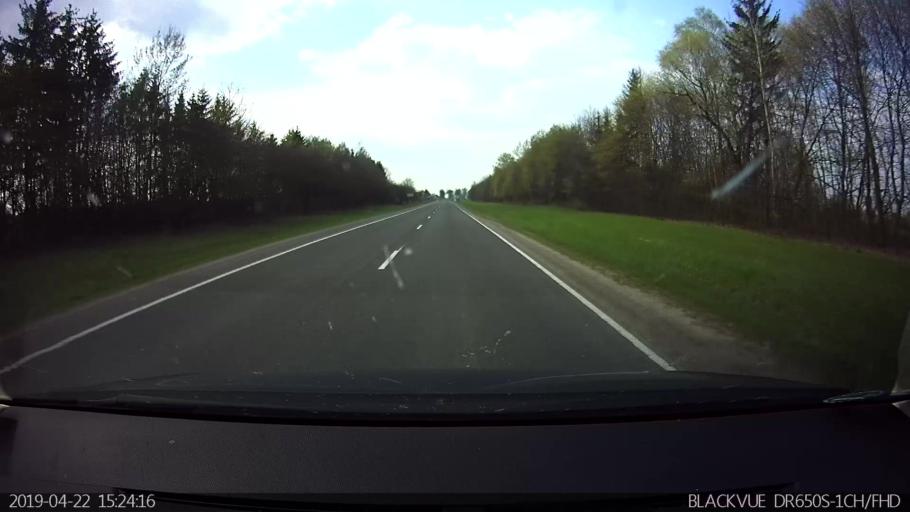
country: BY
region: Brest
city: Vysokaye
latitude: 52.3599
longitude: 23.4109
